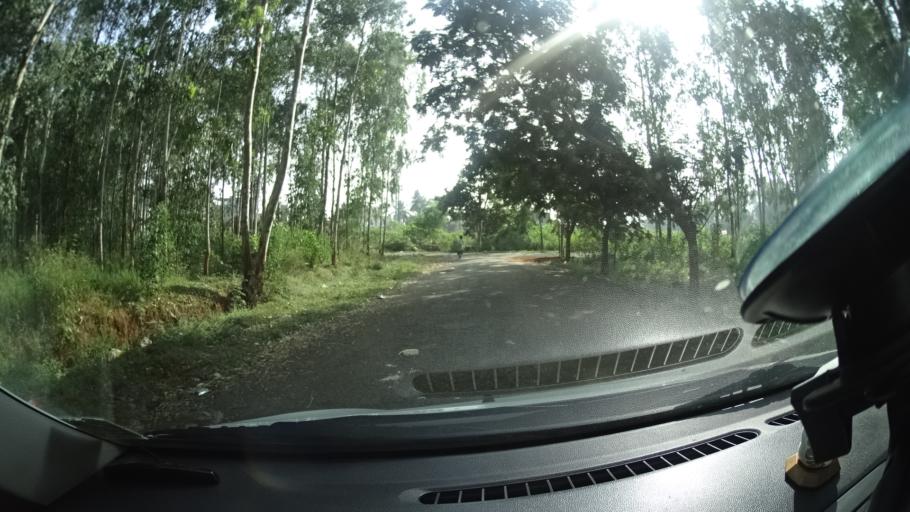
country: IN
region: Karnataka
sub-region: Bangalore Urban
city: Yelahanka
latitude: 13.0780
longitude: 77.5902
